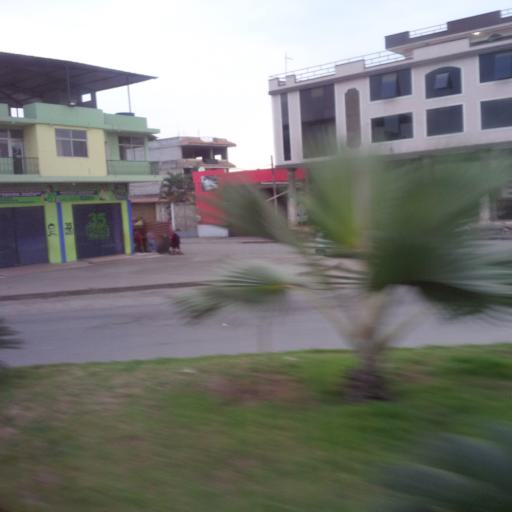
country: EC
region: Canar
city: La Troncal
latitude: -2.3344
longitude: -79.3981
